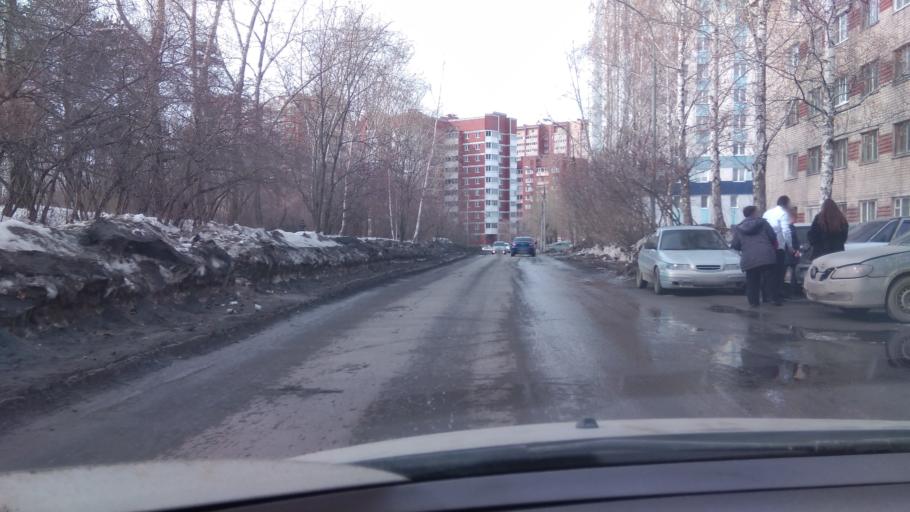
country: RU
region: Sverdlovsk
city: Sovkhoznyy
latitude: 56.7653
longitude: 60.6093
